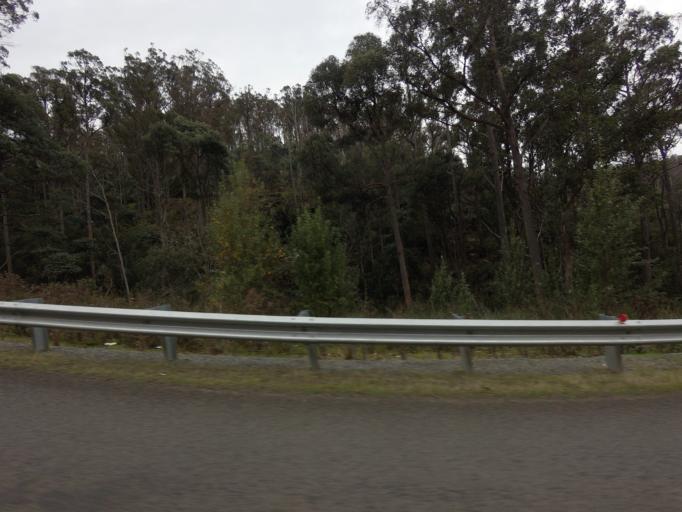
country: AU
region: Tasmania
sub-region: Derwent Valley
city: New Norfolk
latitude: -42.5870
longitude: 147.0142
